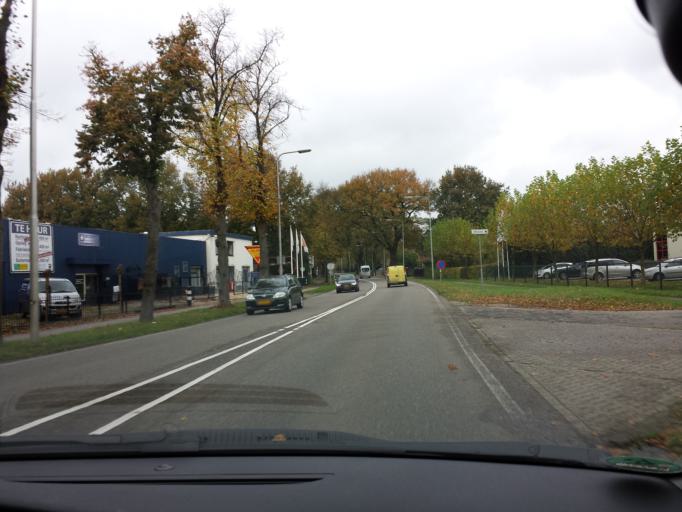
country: NL
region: North Brabant
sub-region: Gemeente Cuijk
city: Cuijk
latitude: 51.7587
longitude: 5.8714
